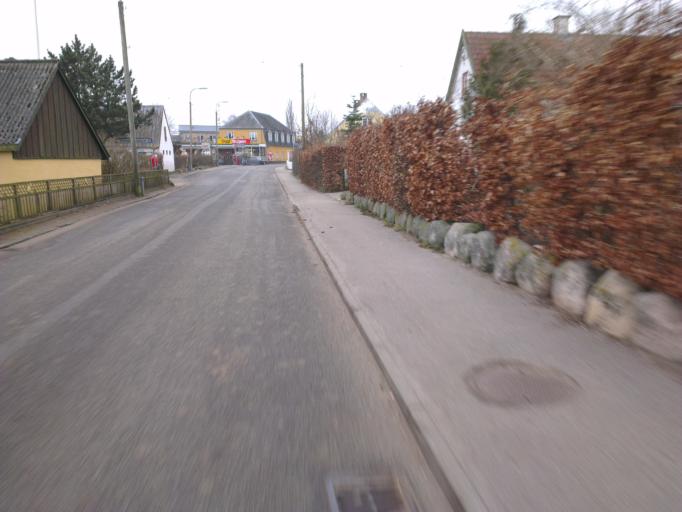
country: DK
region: Capital Region
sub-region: Frederikssund Kommune
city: Skibby
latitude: 55.7836
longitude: 12.0182
